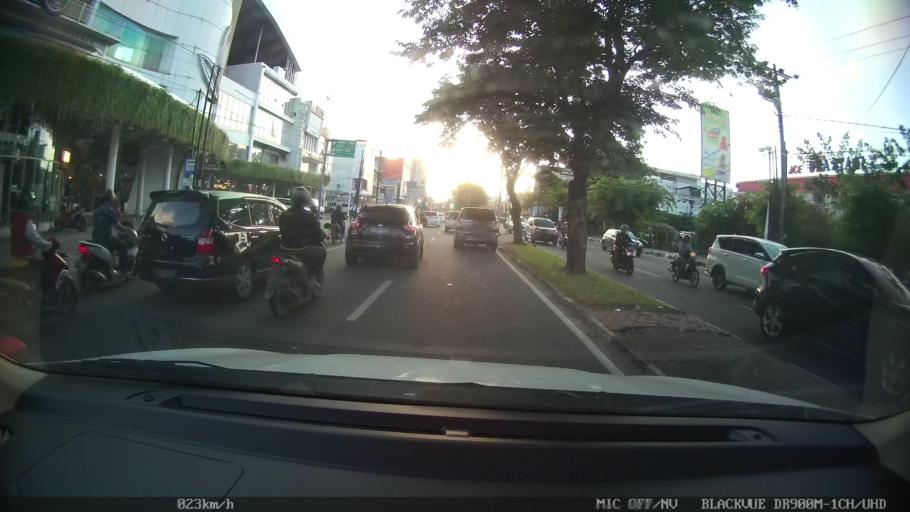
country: ID
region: North Sumatra
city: Medan
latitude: 3.5901
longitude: 98.6551
